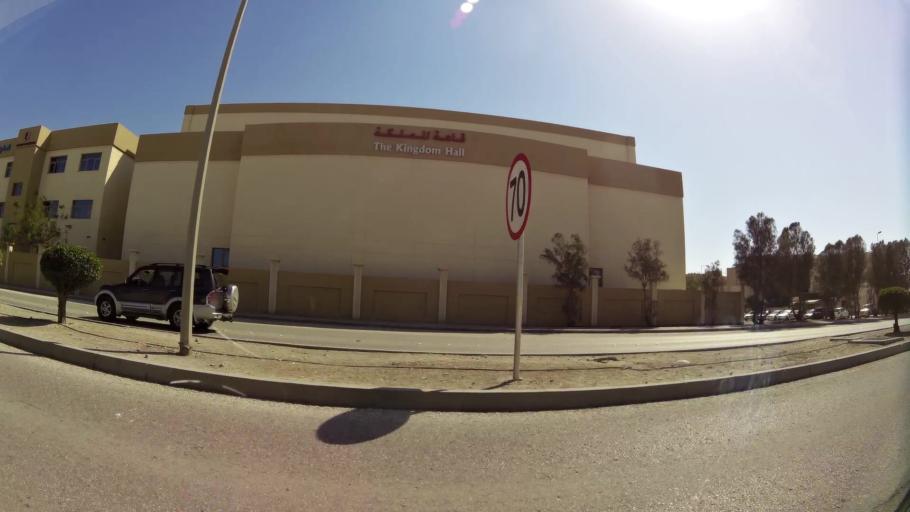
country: BH
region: Manama
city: Manama
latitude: 26.2126
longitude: 50.5720
